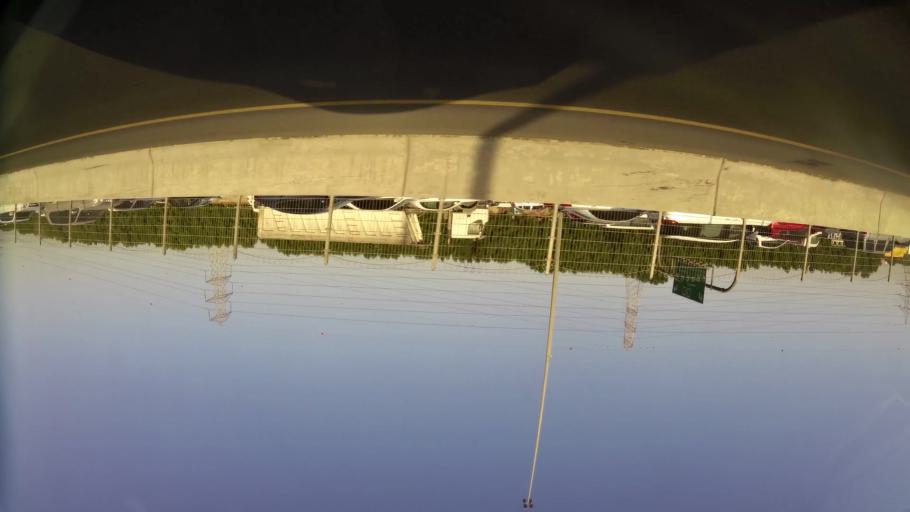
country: AE
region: Ash Shariqah
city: Sharjah
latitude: 25.2485
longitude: 55.4052
